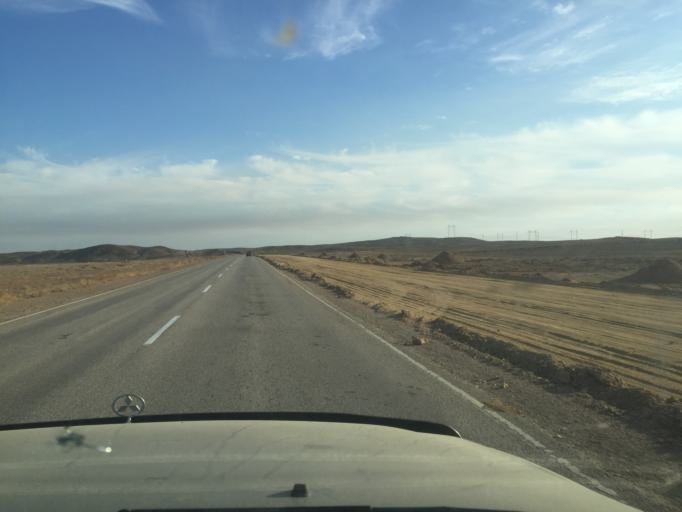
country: KZ
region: Zhambyl
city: Mynaral
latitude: 45.5174
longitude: 73.4916
